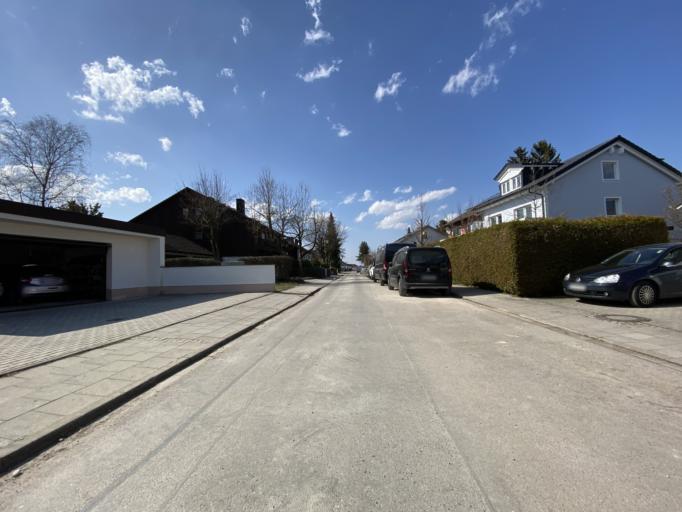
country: DE
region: Bavaria
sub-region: Upper Bavaria
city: Aschheim
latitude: 48.1536
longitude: 11.6867
